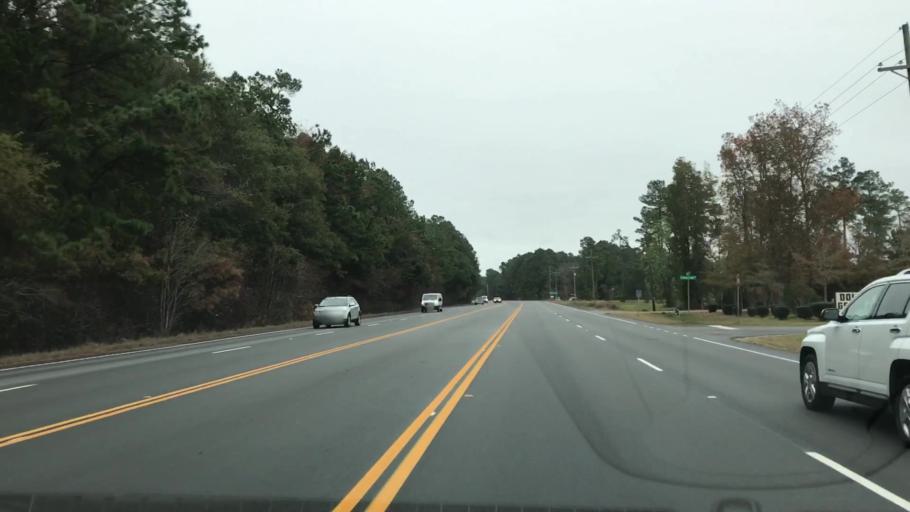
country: US
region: South Carolina
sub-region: Charleston County
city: Awendaw
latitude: 33.0979
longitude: -79.4720
